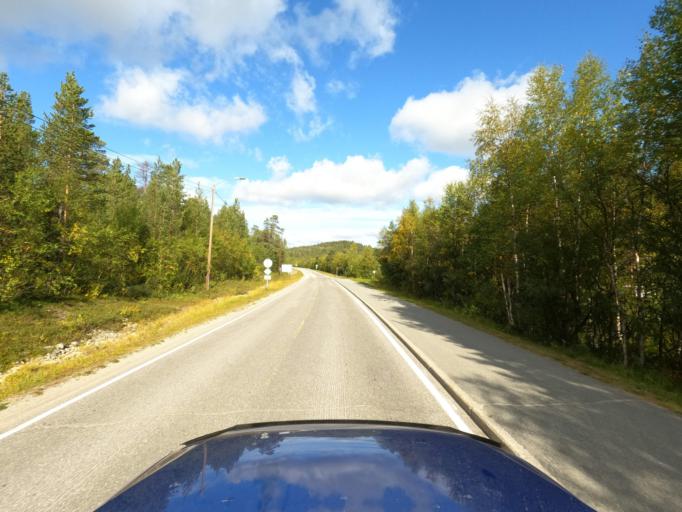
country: NO
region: Finnmark Fylke
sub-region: Karasjok
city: Karasjohka
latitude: 69.4776
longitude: 25.5170
